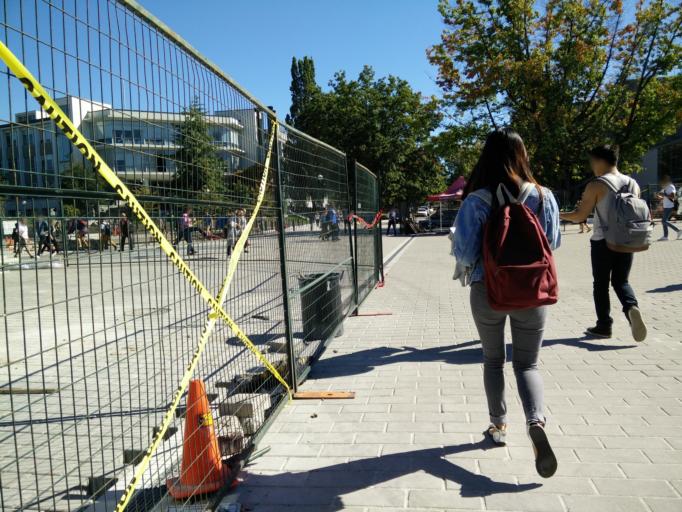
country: CA
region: British Columbia
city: West End
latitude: 49.2658
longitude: -123.2506
